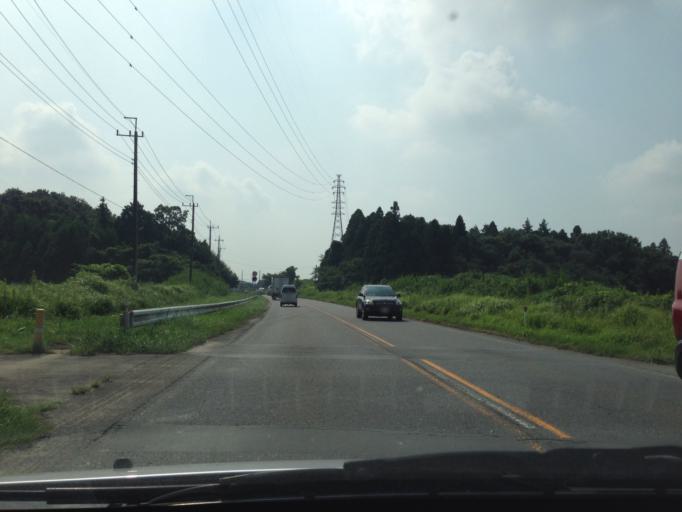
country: JP
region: Ibaraki
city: Ami
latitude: 36.0240
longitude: 140.2378
